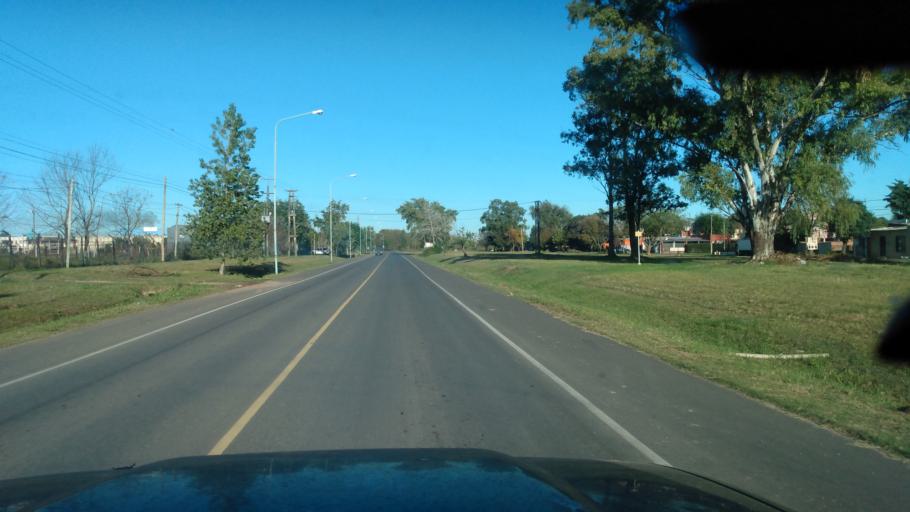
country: AR
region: Buenos Aires
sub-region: Partido de Lujan
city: Lujan
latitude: -34.5627
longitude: -59.1387
